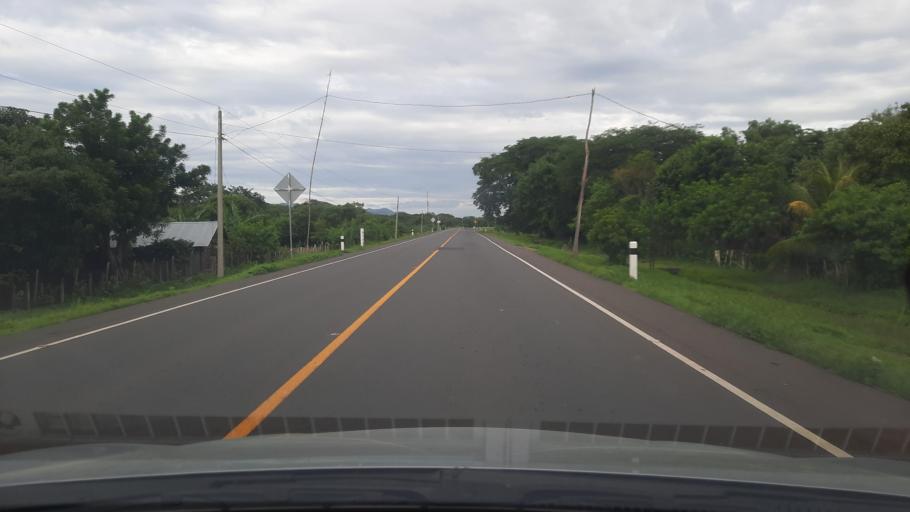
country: NI
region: Leon
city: Telica
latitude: 12.6513
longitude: -86.7509
